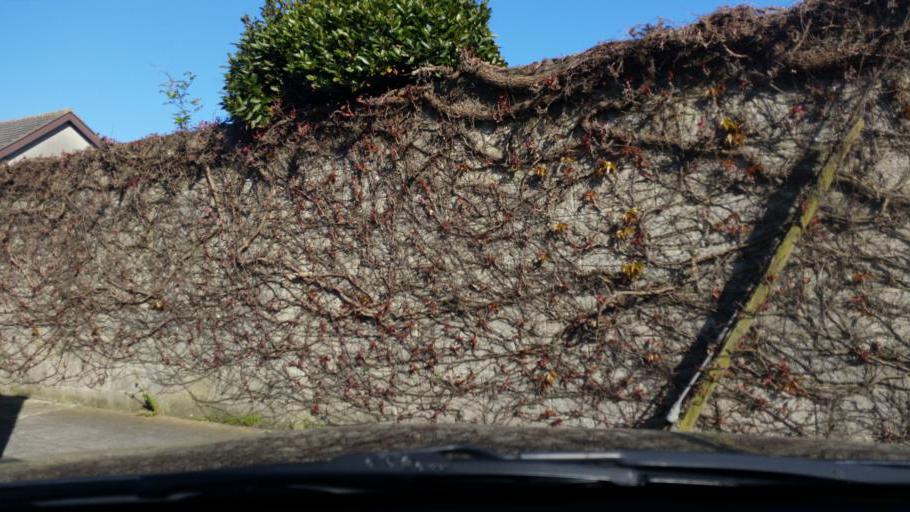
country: IE
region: Leinster
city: Sutton
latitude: 53.3796
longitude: -6.1002
